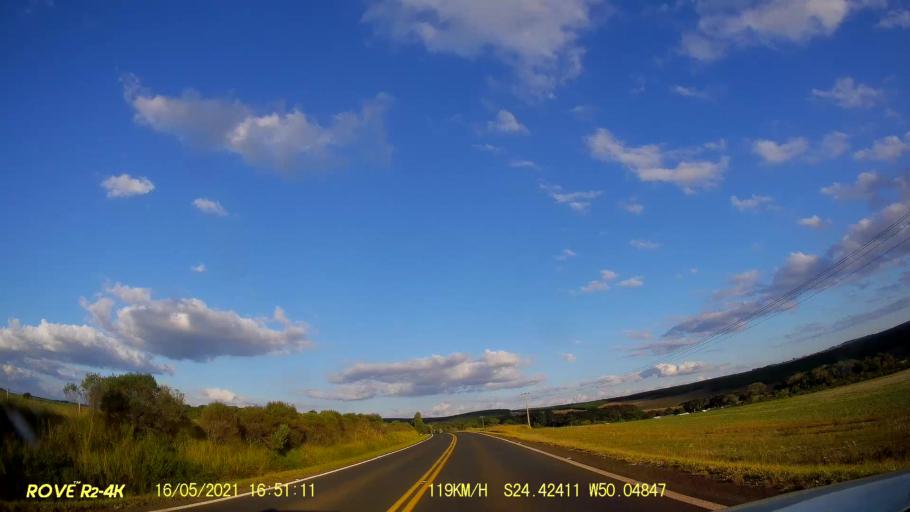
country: BR
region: Parana
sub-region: Pirai Do Sul
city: Pirai do Sul
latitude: -24.4240
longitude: -50.0483
